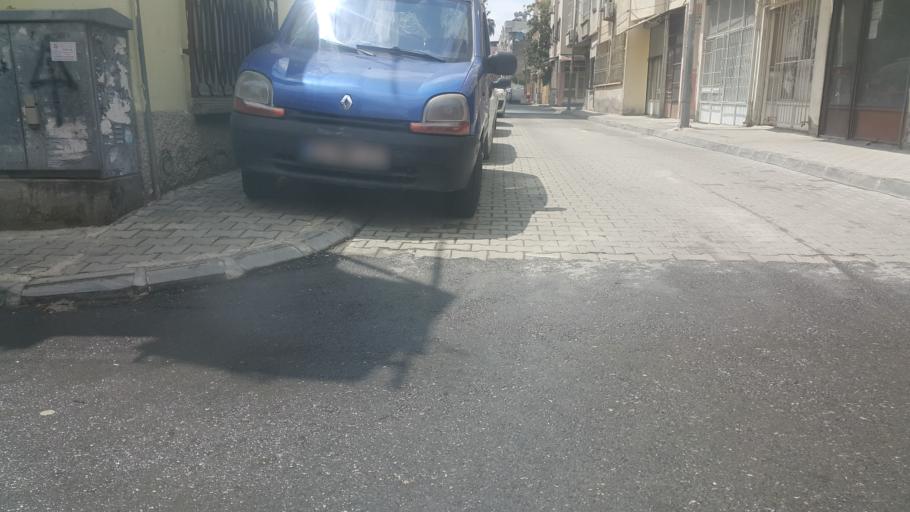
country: TR
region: Mersin
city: Mercin
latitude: 36.8038
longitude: 34.6282
